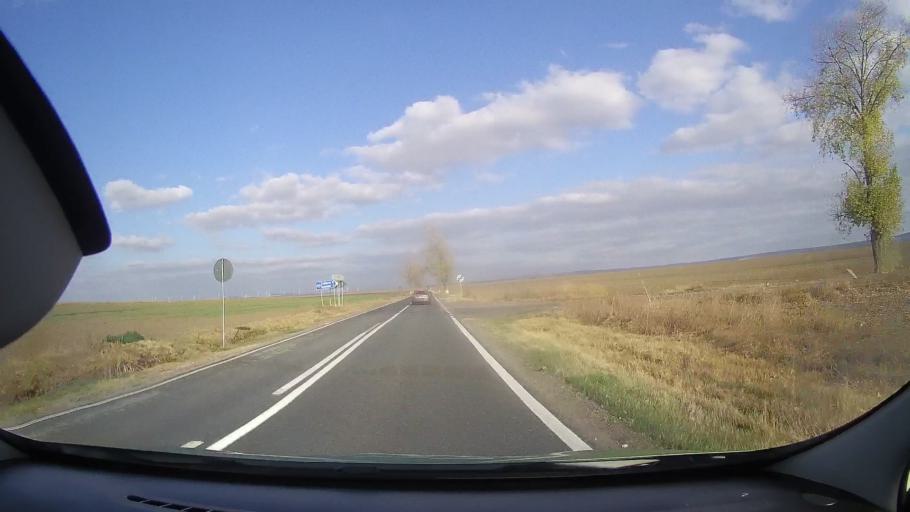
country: RO
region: Tulcea
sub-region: Comuna Topolog
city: Topolog
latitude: 44.8253
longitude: 28.2733
